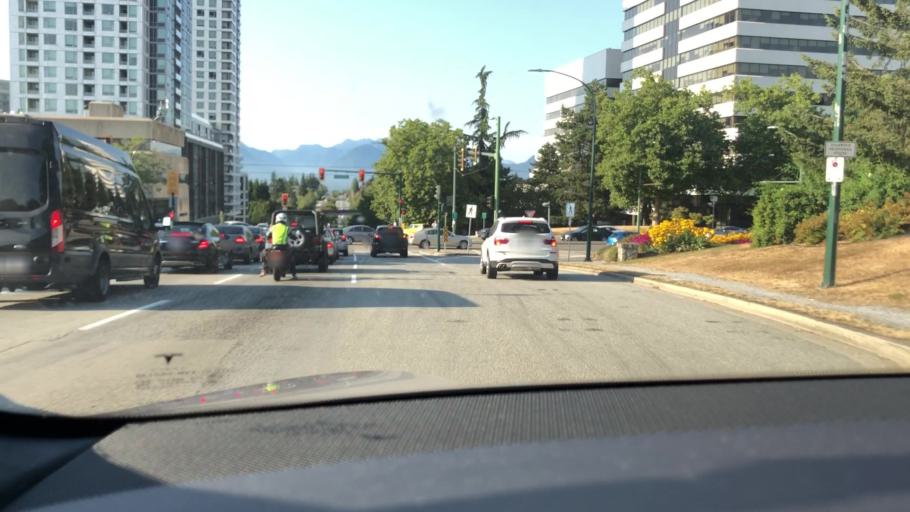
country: CA
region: British Columbia
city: Burnaby
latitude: 49.2318
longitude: -123.0234
